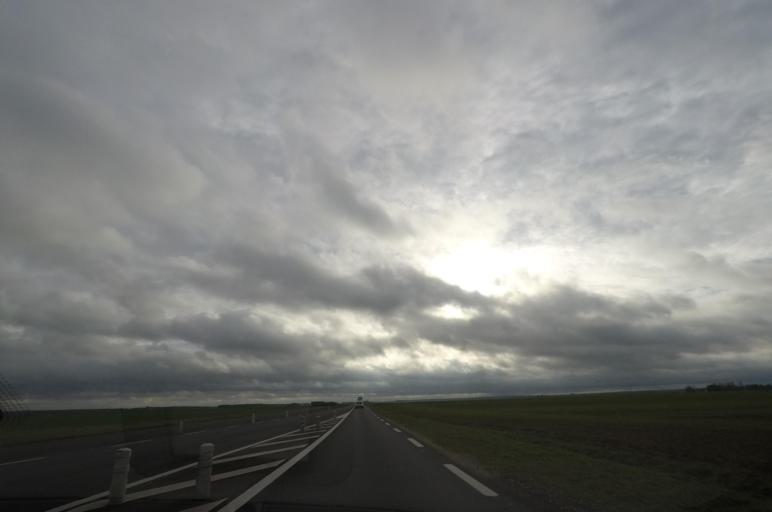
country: FR
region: Centre
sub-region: Departement du Loir-et-Cher
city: Herbault
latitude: 47.7119
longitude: 1.1636
